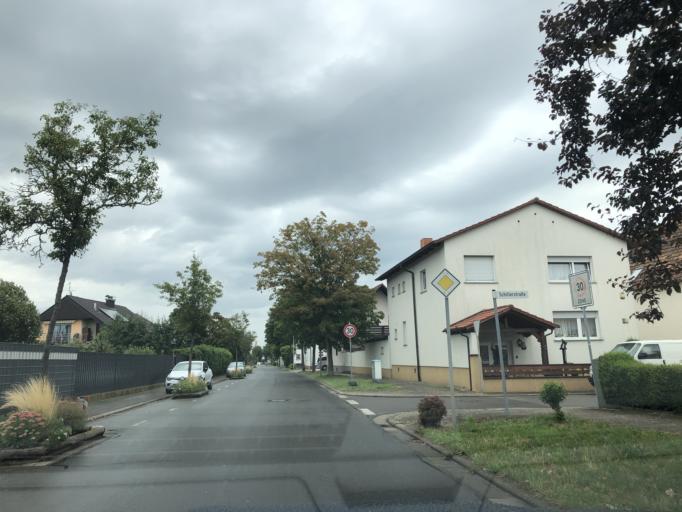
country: DE
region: Rheinland-Pfalz
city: Bellheim
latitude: 49.1978
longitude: 8.2779
